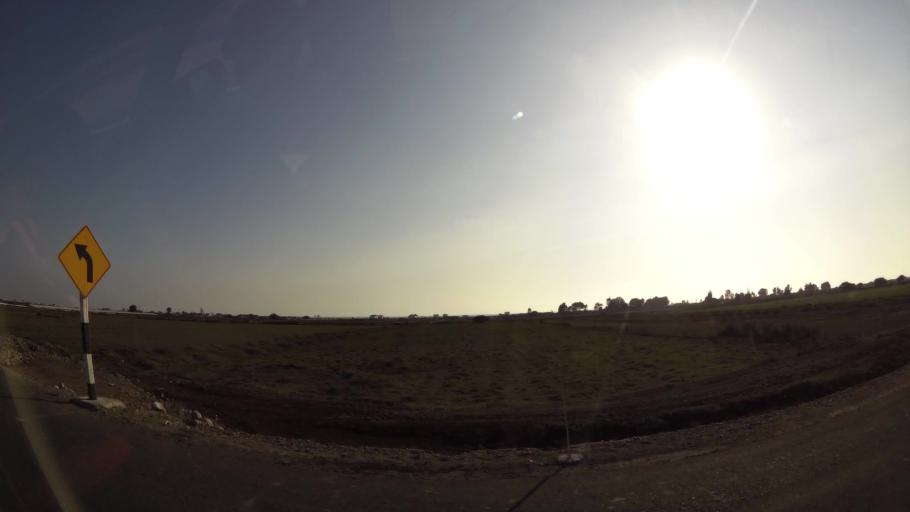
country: PE
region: Ica
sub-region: Provincia de Chincha
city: Chincha Baja
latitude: -13.5586
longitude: -76.1807
